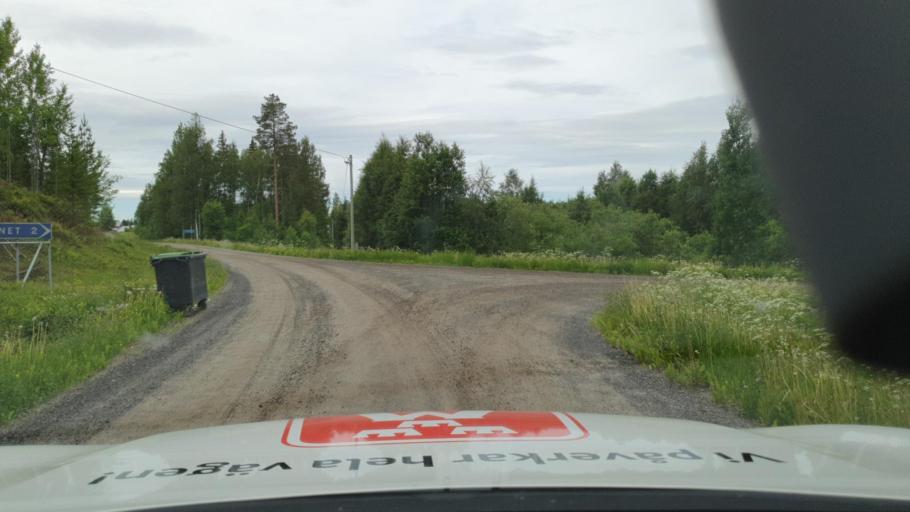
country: SE
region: Vaesterbotten
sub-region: Skelleftea Kommun
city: Burtraesk
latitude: 64.3897
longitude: 20.6114
